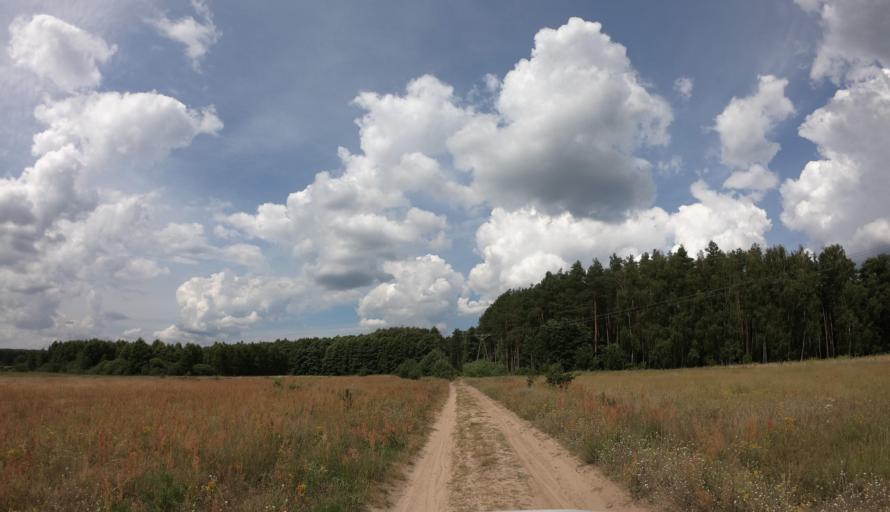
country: PL
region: West Pomeranian Voivodeship
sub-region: Powiat stargardzki
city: Kobylanka
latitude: 53.3265
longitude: 14.8199
